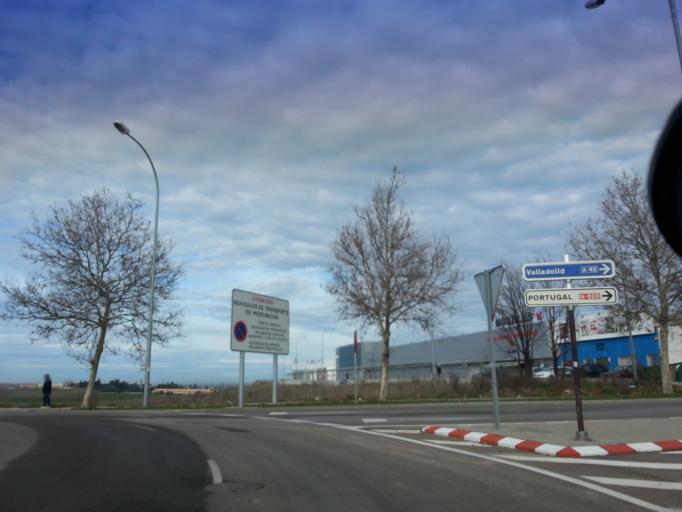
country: ES
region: Castille and Leon
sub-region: Provincia de Salamanca
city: Villares de la Reina
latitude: 40.9879
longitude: -5.6464
